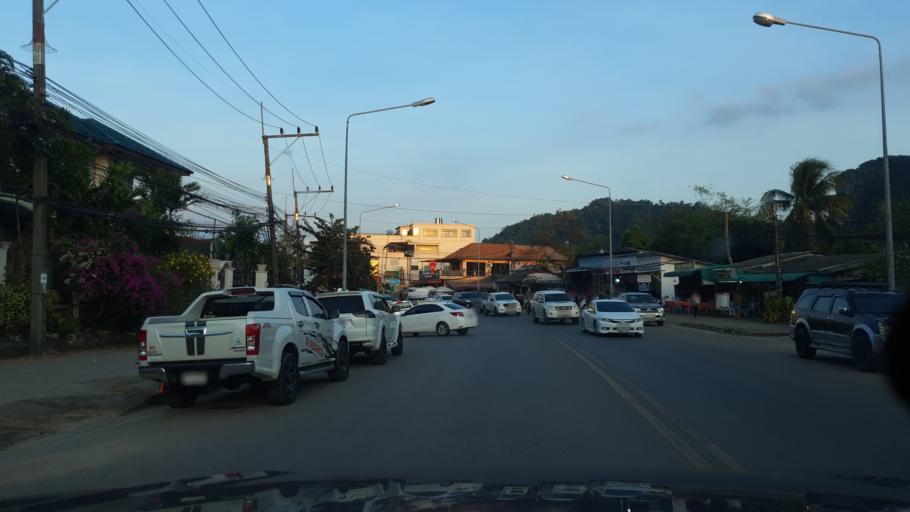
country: TH
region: Phangnga
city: Ban Ao Nang
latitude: 8.0352
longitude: 98.8321
